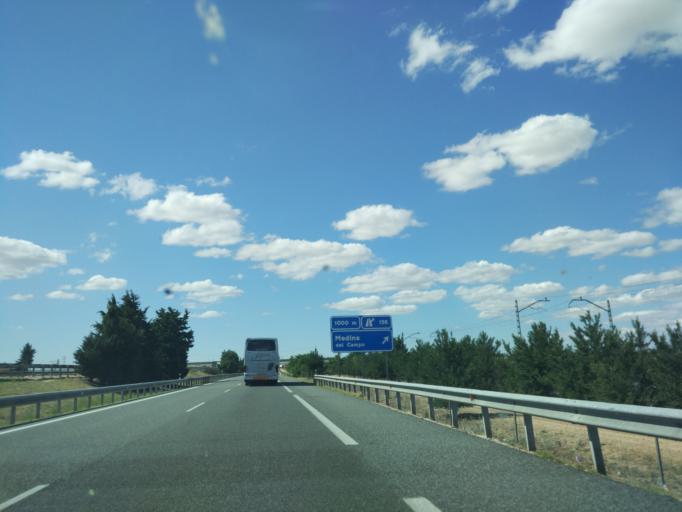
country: ES
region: Castille and Leon
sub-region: Provincia de Valladolid
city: Medina del Campo
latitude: 41.2819
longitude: -4.8934
